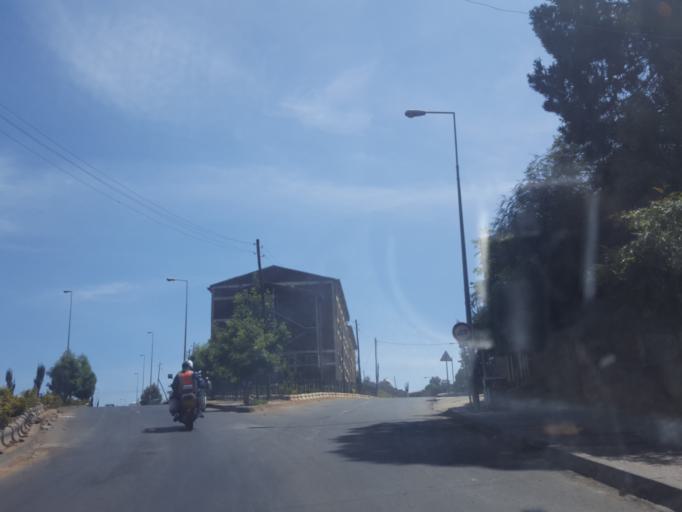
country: ET
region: Adis Abeba
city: Addis Ababa
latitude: 9.0636
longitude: 38.7296
